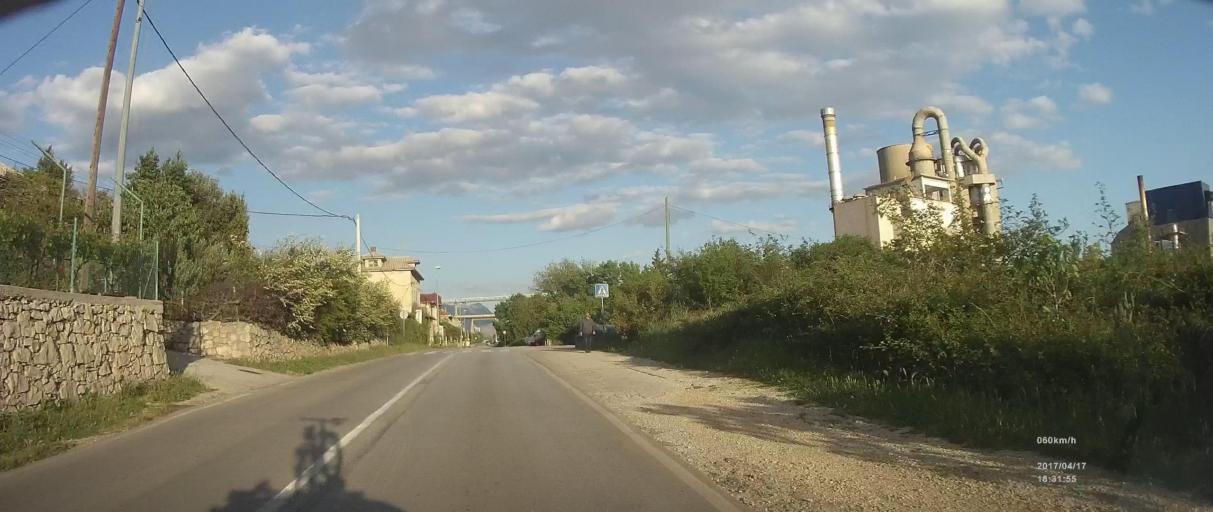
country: HR
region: Splitsko-Dalmatinska
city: Vranjic
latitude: 43.5439
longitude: 16.4397
